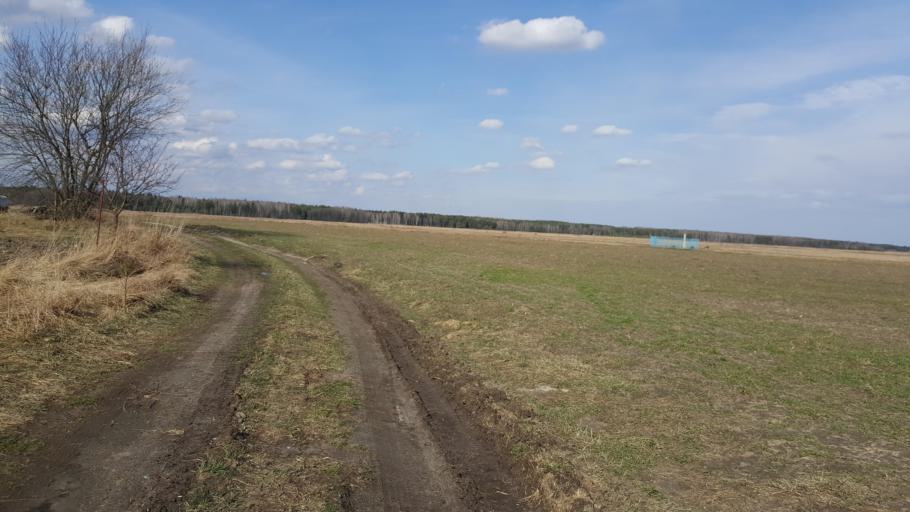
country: BY
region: Brest
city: Kamyanyets
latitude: 52.4011
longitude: 23.9622
